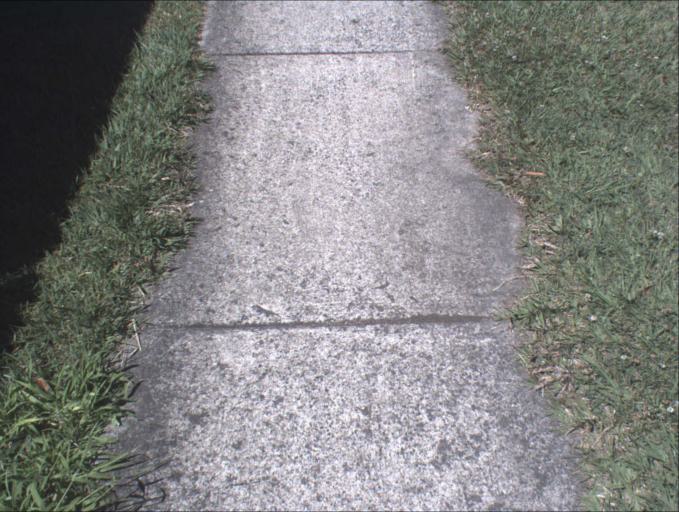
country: AU
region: Queensland
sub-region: Logan
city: Logan City
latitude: -27.6351
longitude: 153.1245
